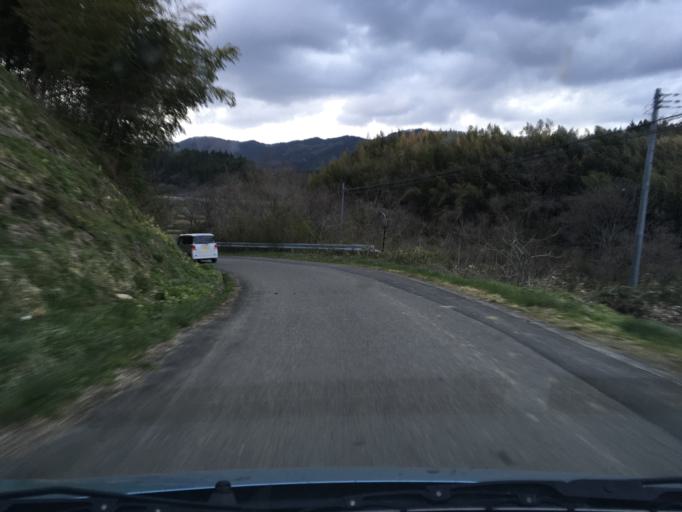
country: JP
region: Iwate
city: Ichinoseki
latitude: 38.9684
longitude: 141.2103
